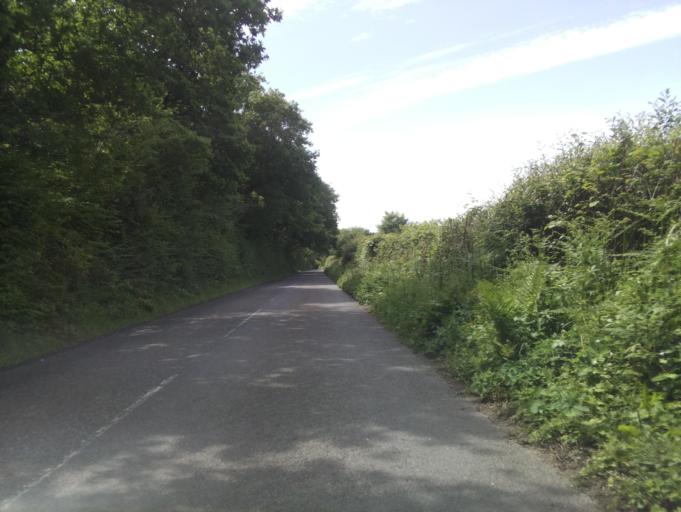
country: GB
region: England
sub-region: Devon
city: Kingsbridge
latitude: 50.3617
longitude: -3.7606
